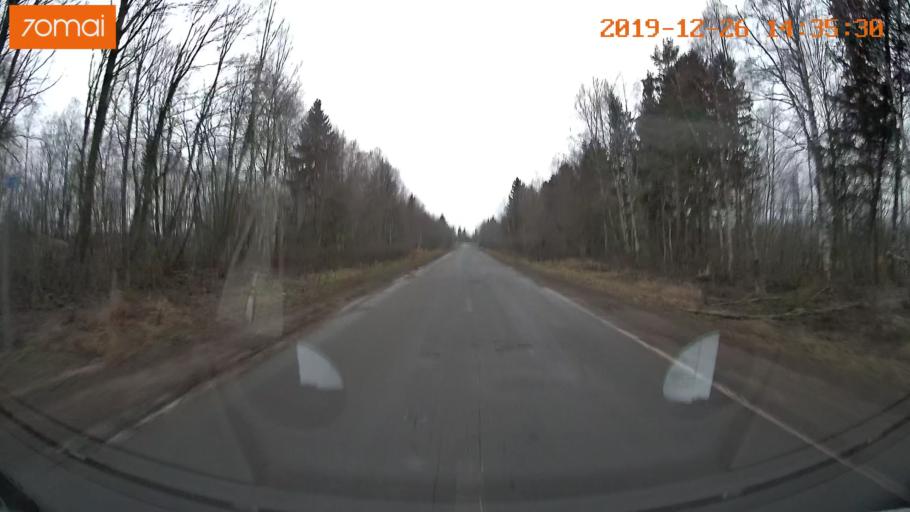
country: RU
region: Jaroslavl
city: Poshekhon'ye
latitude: 58.4197
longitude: 38.9837
